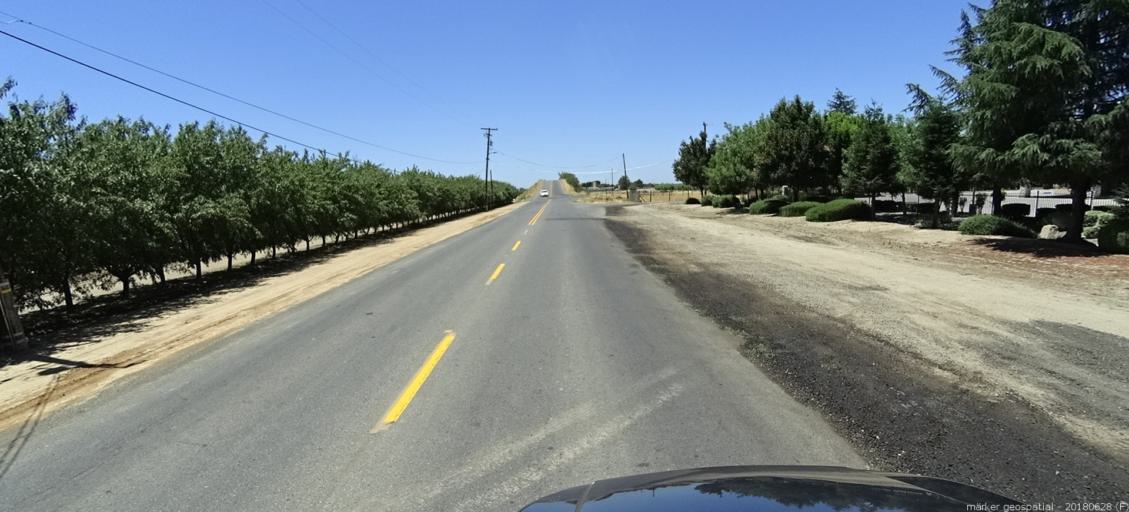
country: US
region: California
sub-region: Madera County
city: Parksdale
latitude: 36.9381
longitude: -120.0310
